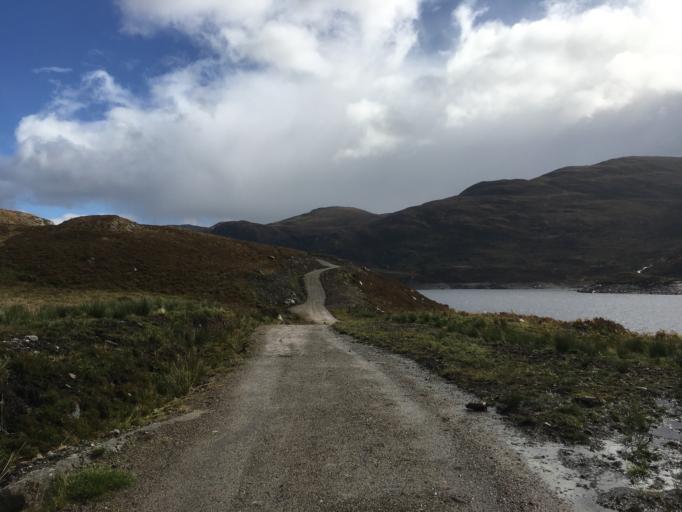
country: GB
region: Scotland
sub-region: Highland
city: Spean Bridge
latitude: 57.3409
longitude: -4.9737
